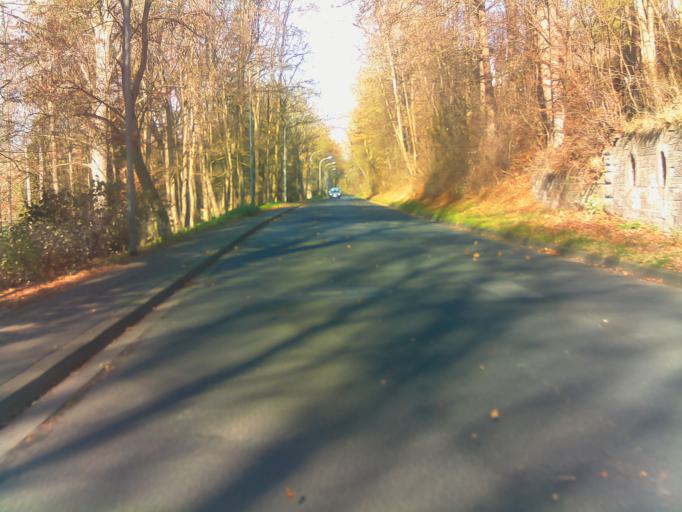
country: DE
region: Bavaria
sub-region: Regierungsbezirk Unterfranken
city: Bad Kissingen
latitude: 50.2098
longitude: 10.0727
